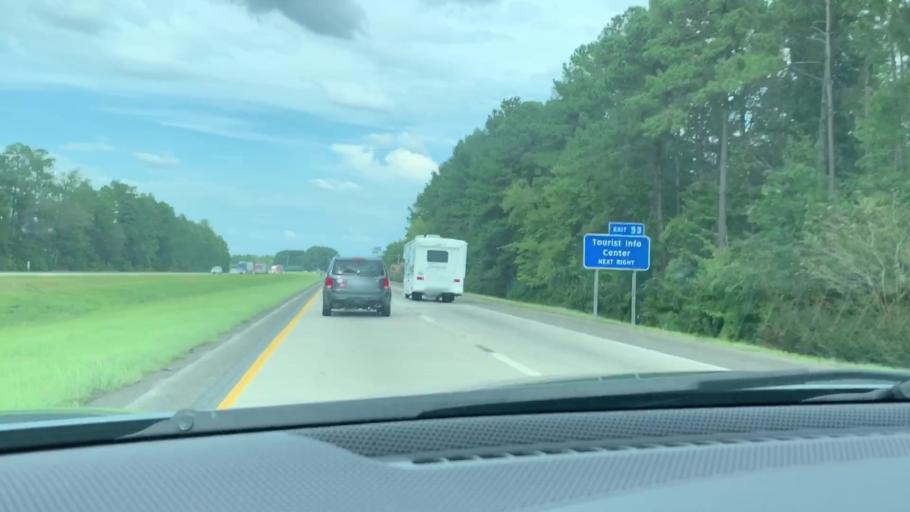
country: US
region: South Carolina
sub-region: Colleton County
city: Walterboro
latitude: 32.8719
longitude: -80.7201
